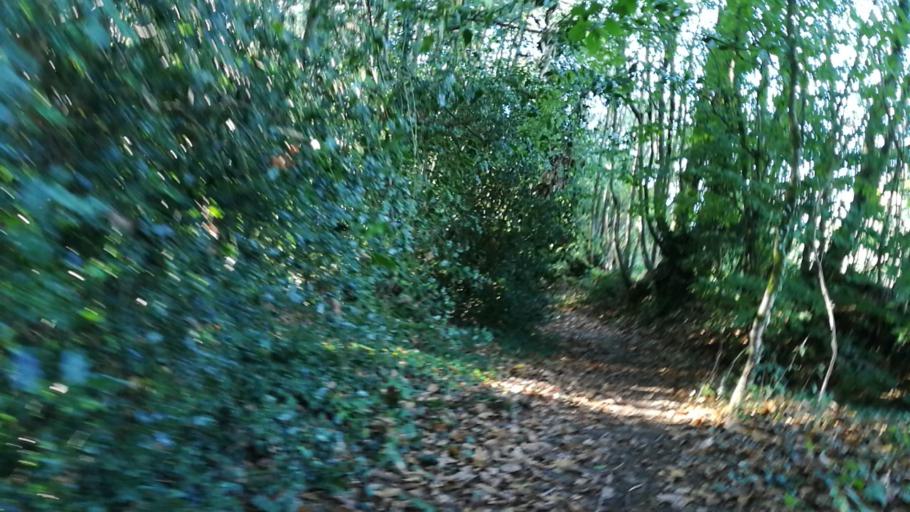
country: FR
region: Brittany
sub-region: Departement d'Ille-et-Vilaine
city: Retiers
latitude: 47.9142
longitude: -1.4047
